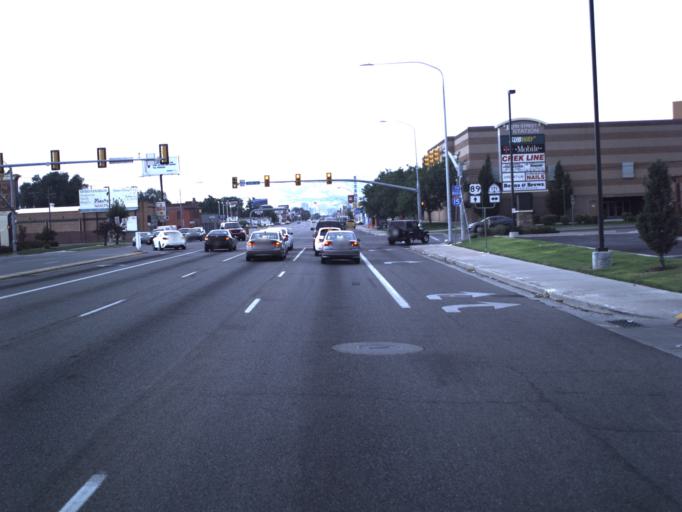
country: US
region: Utah
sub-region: Salt Lake County
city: Centerfield
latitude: 40.6991
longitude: -111.8882
